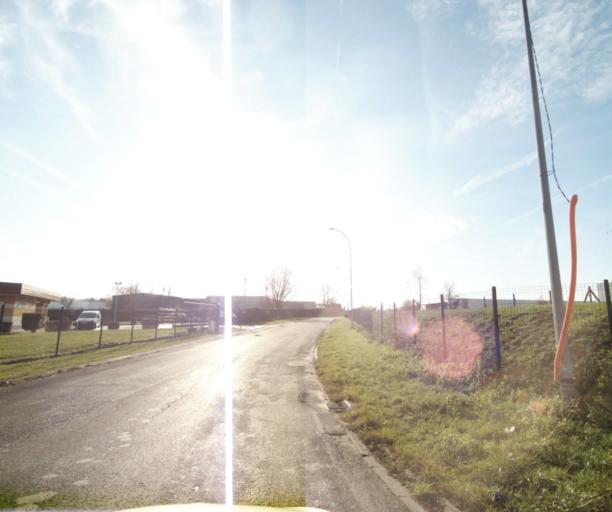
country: FR
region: Nord-Pas-de-Calais
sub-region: Departement du Nord
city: Saultain
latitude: 50.3467
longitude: 3.5661
